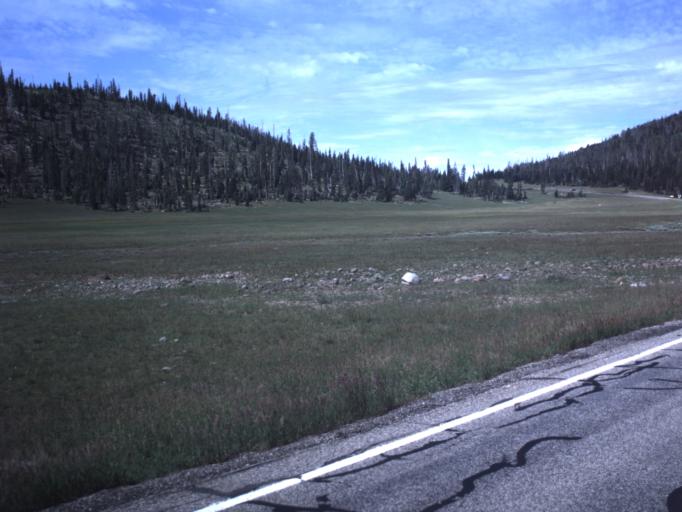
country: US
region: Utah
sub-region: Iron County
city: Cedar City
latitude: 37.5722
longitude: -112.8316
